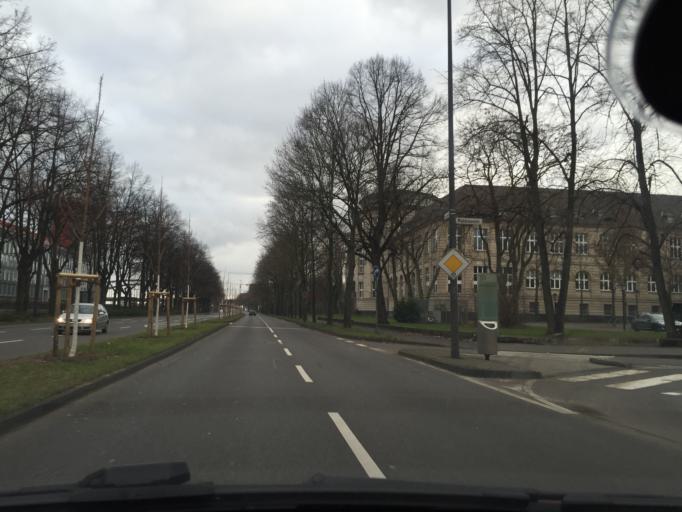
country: DE
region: North Rhine-Westphalia
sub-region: Regierungsbezirk Koln
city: Bayenthal
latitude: 50.9209
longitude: 6.9678
